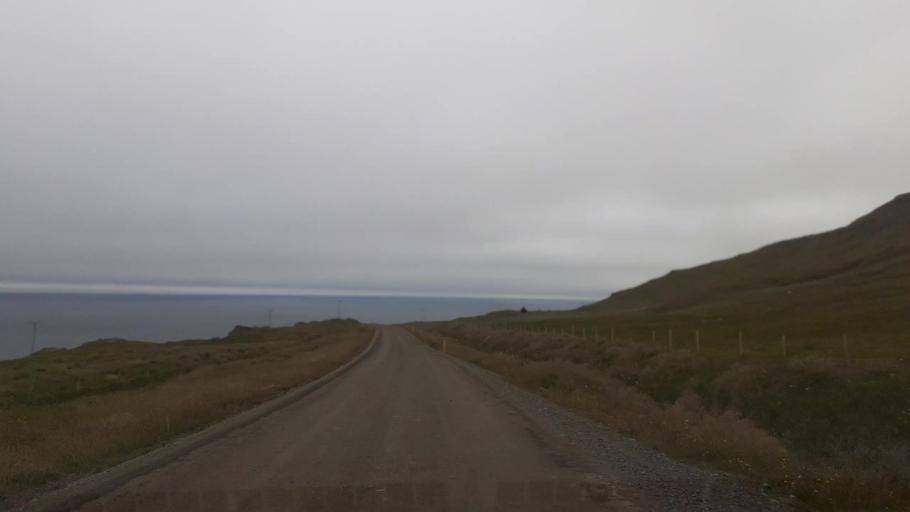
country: IS
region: Northwest
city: Saudarkrokur
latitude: 65.5107
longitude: -20.9709
